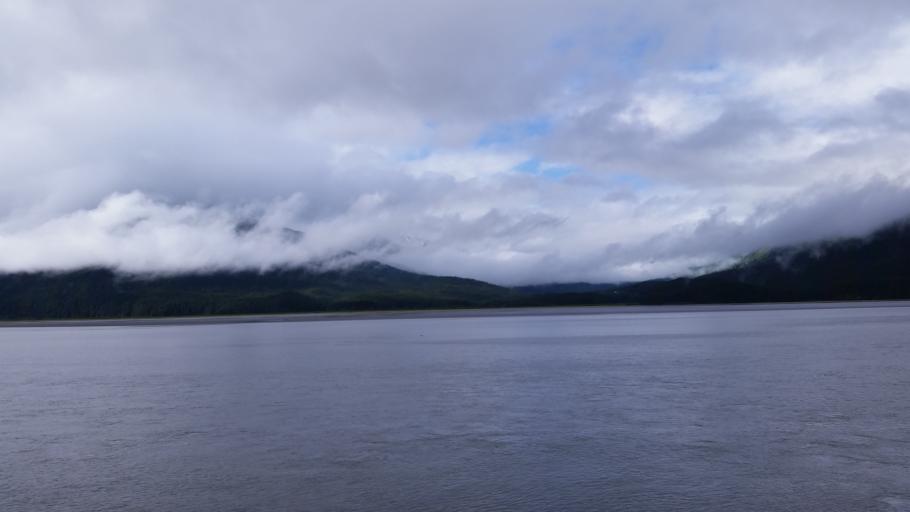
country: US
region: Alaska
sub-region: Anchorage Municipality
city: Girdwood
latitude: 60.8603
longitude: -149.0196
